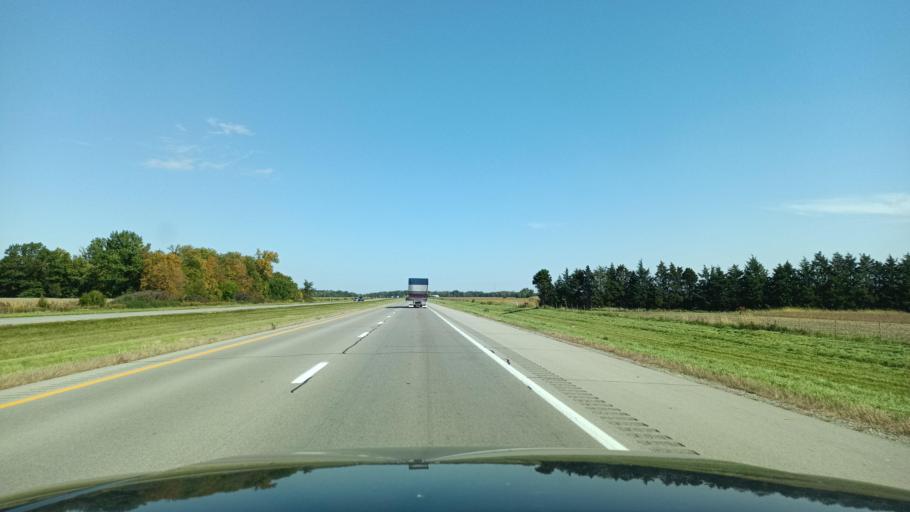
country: US
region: Ohio
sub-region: Henry County
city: Napoleon
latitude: 41.3769
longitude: -84.1813
